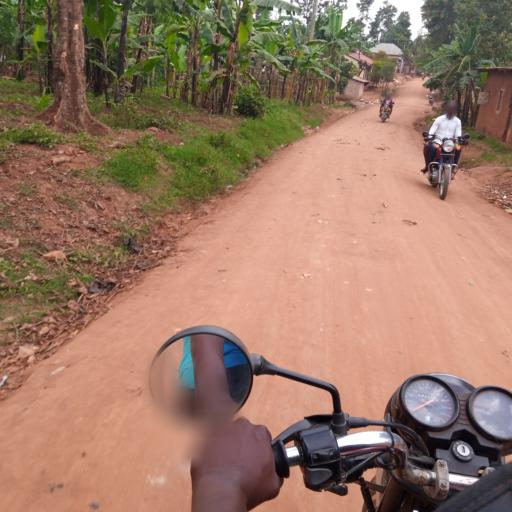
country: UG
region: Eastern Region
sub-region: Mbale District
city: Mbale
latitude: 1.0997
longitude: 34.1799
